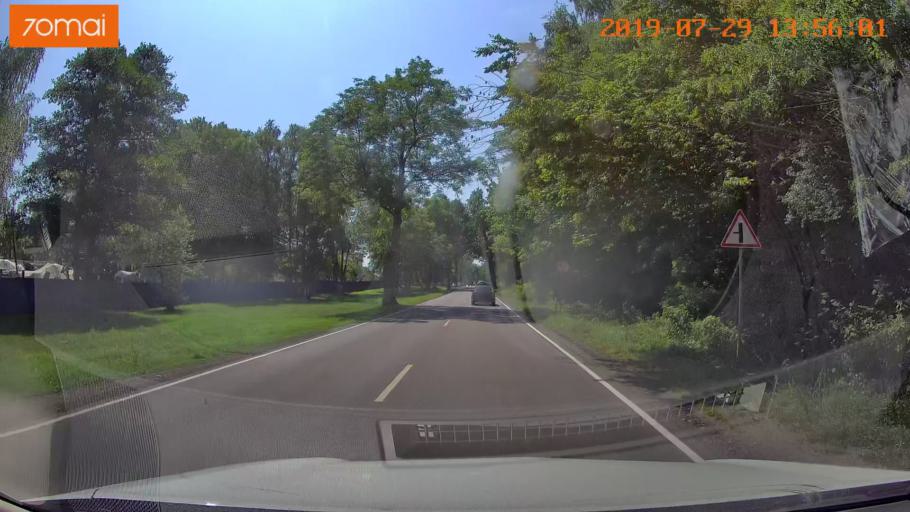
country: RU
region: Kaliningrad
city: Primorsk
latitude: 54.7107
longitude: 19.9519
